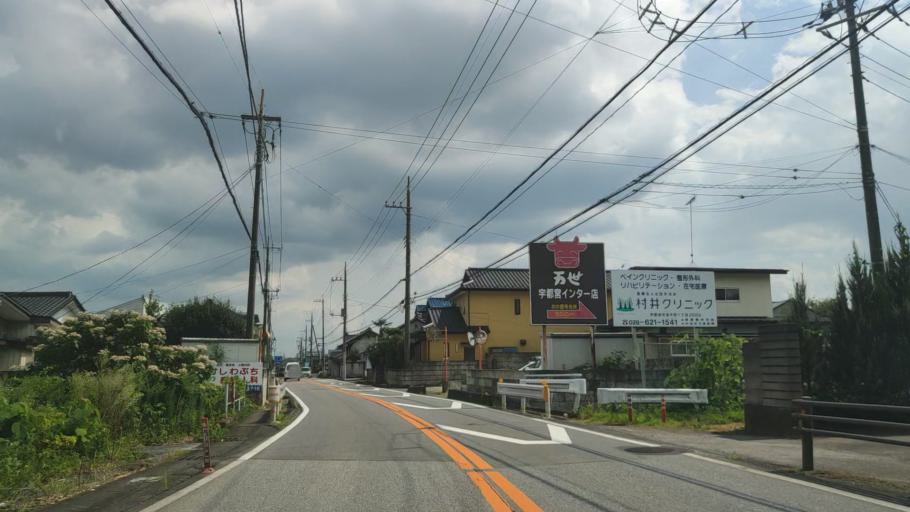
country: JP
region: Tochigi
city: Utsunomiya-shi
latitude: 36.6529
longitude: 139.8420
